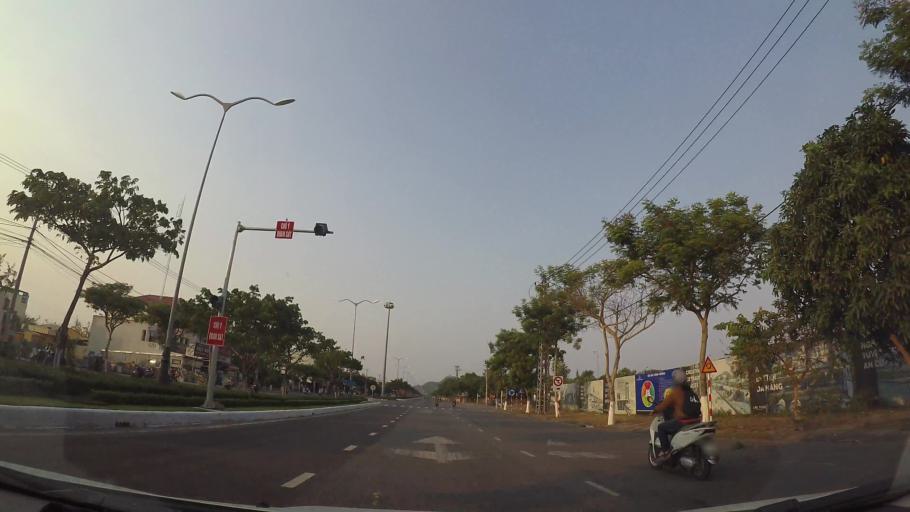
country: VN
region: Da Nang
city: Ngu Hanh Son
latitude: 15.9878
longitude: 108.2572
